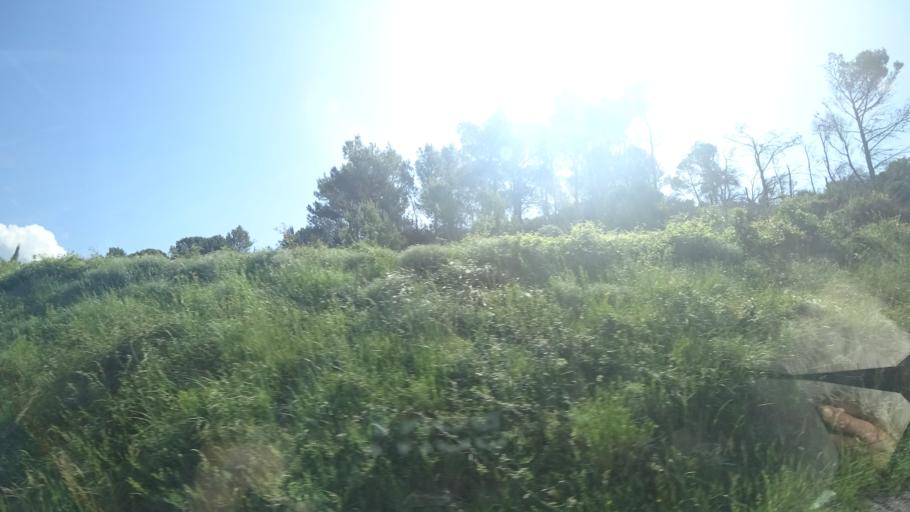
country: FR
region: Languedoc-Roussillon
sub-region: Departement de l'Herault
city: Olonzac
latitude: 43.3482
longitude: 2.7415
